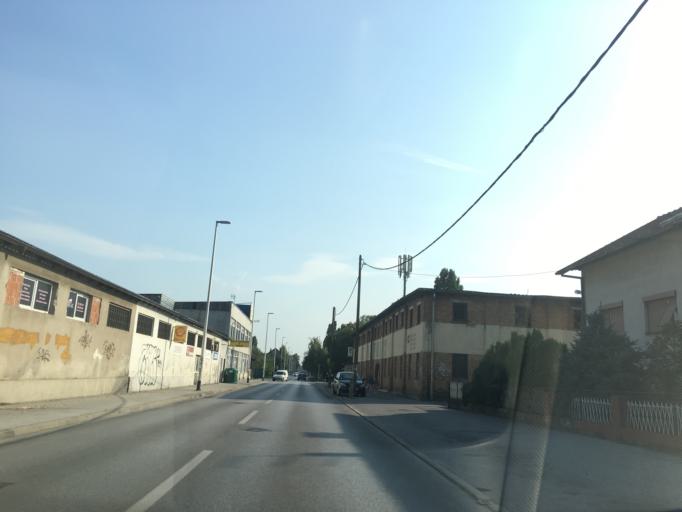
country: HR
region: Grad Zagreb
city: Jankomir
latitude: 45.8082
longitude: 15.9300
